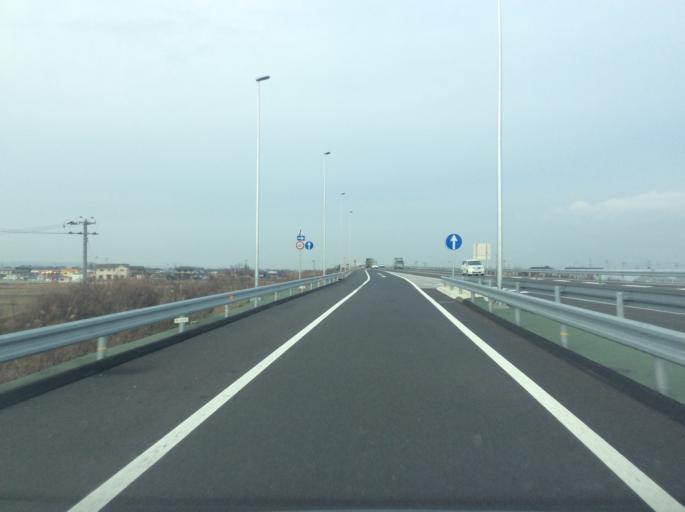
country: JP
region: Miyagi
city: Watari
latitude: 38.0403
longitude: 140.8927
